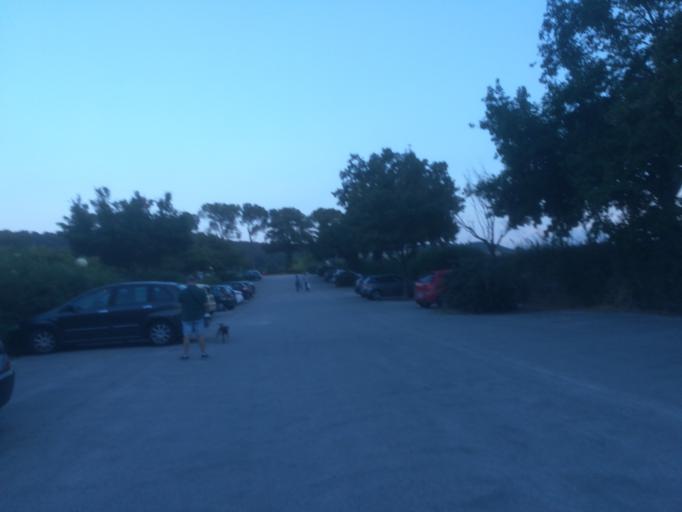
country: IT
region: The Marches
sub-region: Provincia di Macerata
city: Casette Verdini
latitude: 43.2200
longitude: 13.4055
